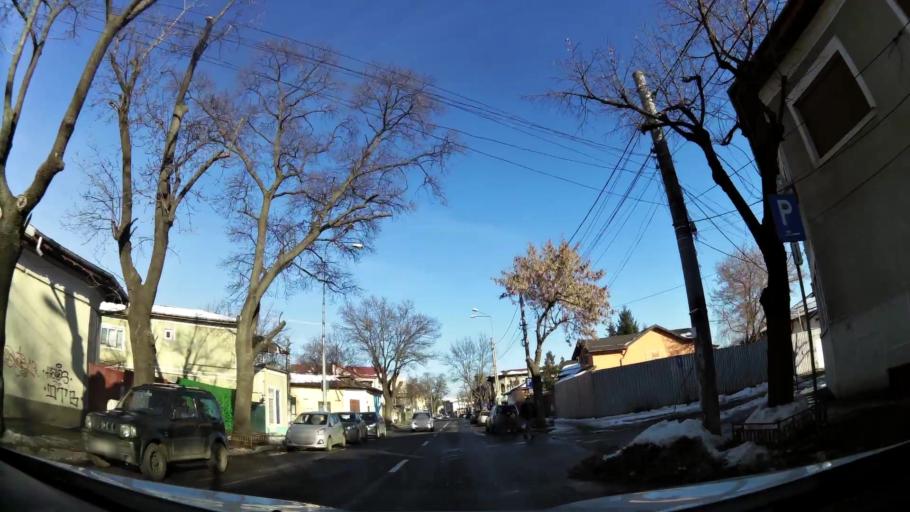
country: RO
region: Bucuresti
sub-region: Municipiul Bucuresti
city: Bucuresti
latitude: 44.4010
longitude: 26.0894
